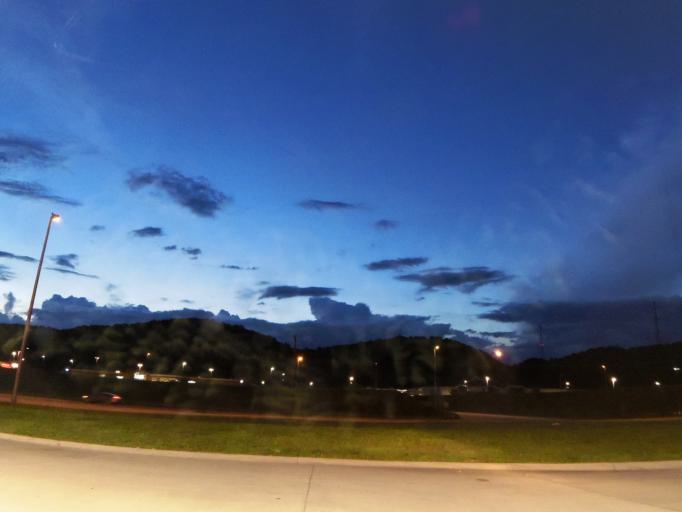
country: US
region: Tennessee
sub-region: Roane County
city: Midtown
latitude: 35.8906
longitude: -84.5476
